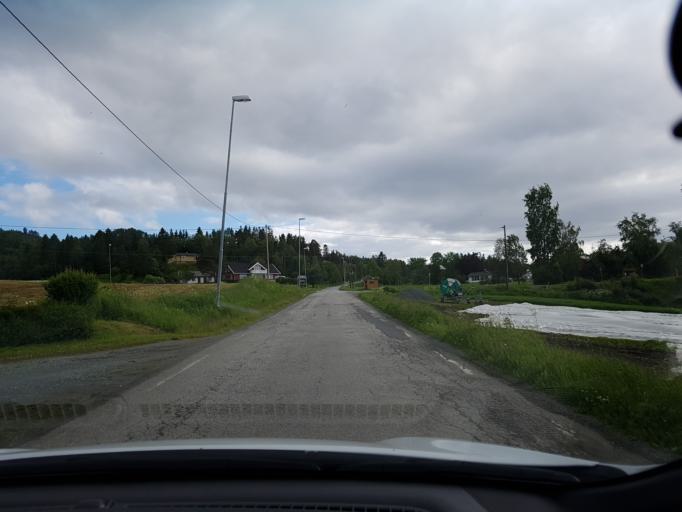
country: NO
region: Nord-Trondelag
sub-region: Frosta
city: Frosta
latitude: 63.6242
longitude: 10.7640
